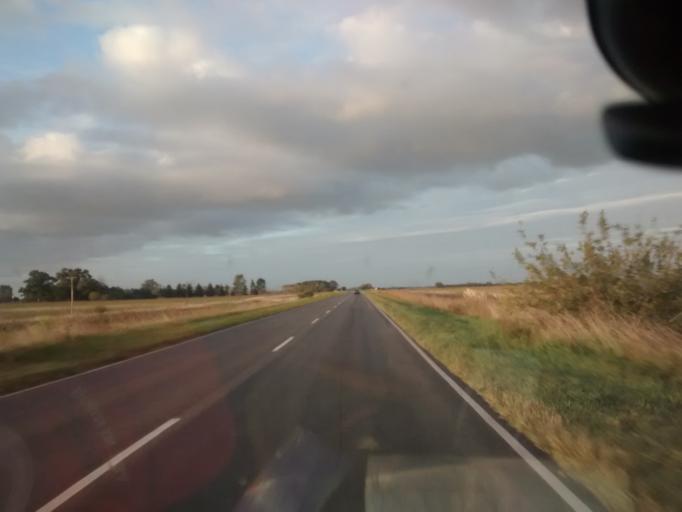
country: AR
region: Buenos Aires
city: Ranchos
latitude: -35.5507
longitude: -58.3878
